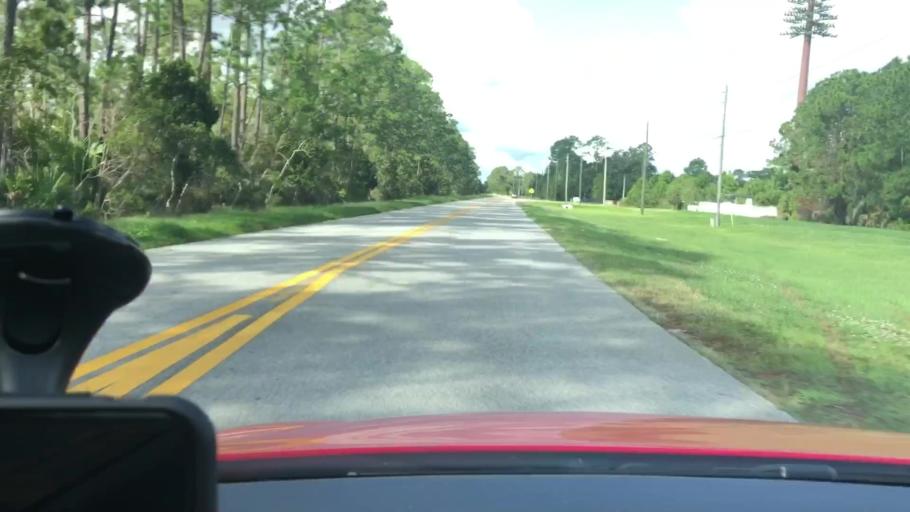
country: US
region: Florida
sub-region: Volusia County
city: Holly Hill
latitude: 29.2371
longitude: -81.0927
